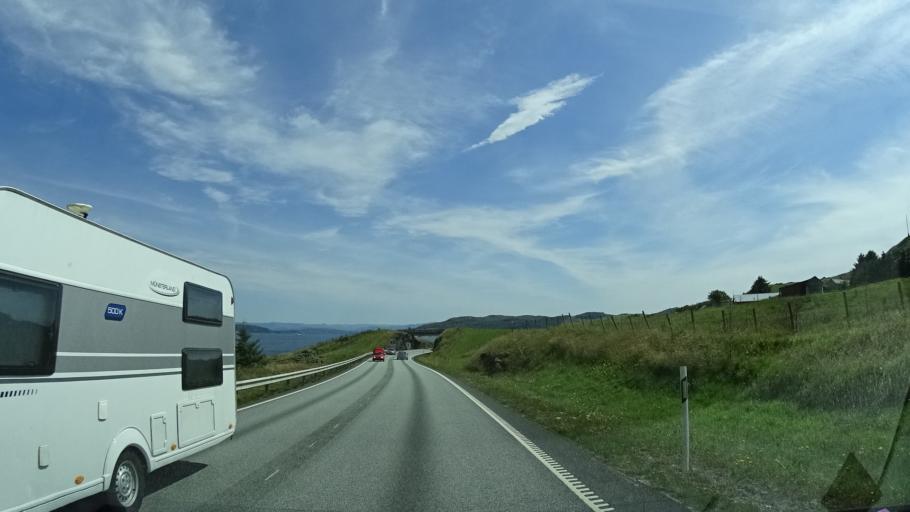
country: NO
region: Rogaland
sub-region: Rennesoy
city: Vikevag
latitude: 59.1251
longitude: 5.6665
